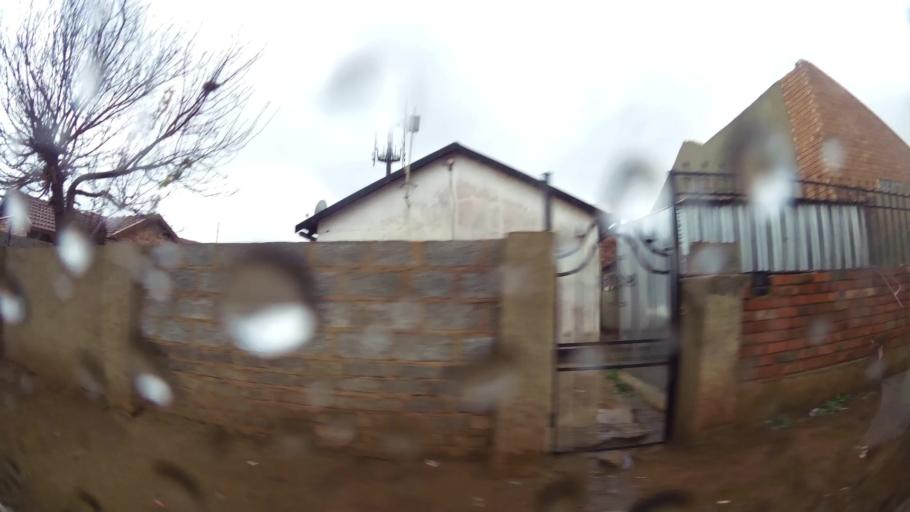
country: ZA
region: Gauteng
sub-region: Ekurhuleni Metropolitan Municipality
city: Germiston
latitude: -26.3647
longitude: 28.1329
